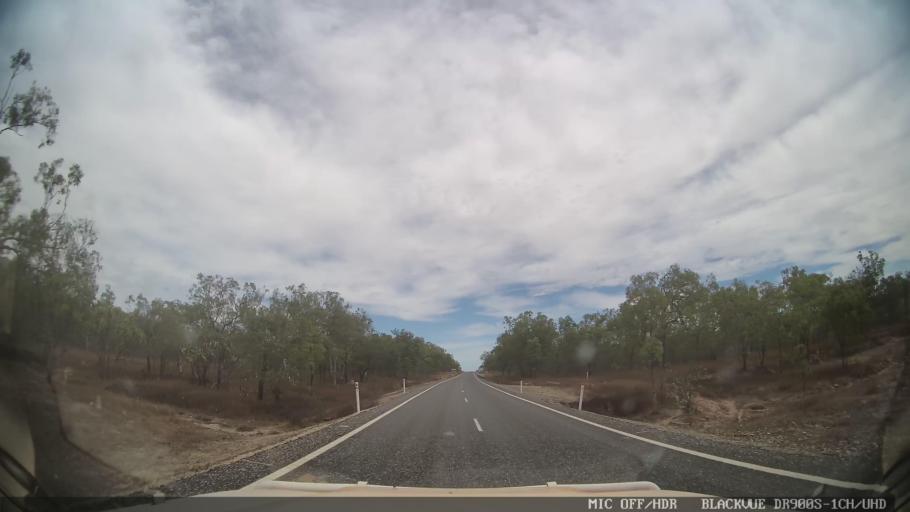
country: AU
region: Queensland
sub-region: Cairns
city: Port Douglas
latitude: -16.2541
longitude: 144.7252
